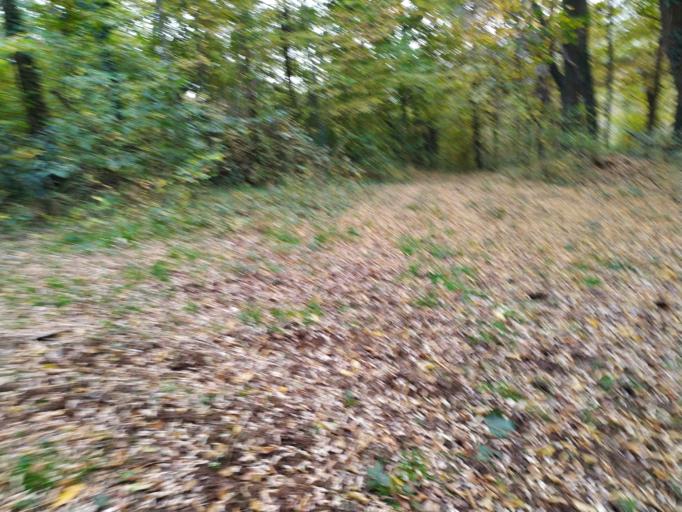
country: IT
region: Veneto
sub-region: Provincia di Vicenza
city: Schio
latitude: 45.6871
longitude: 11.3604
